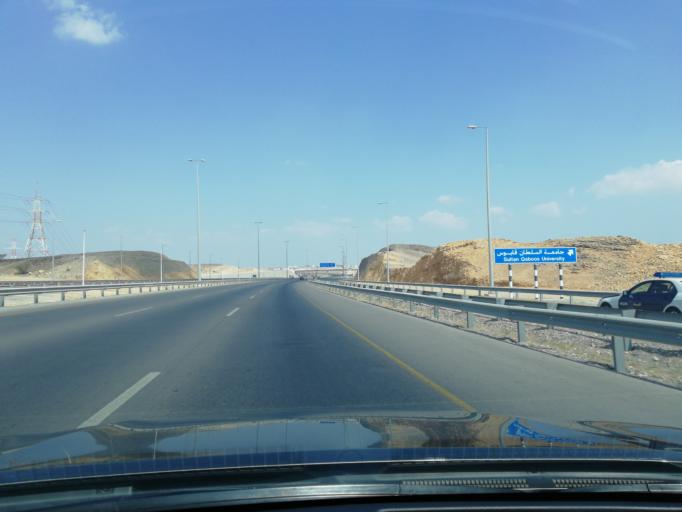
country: OM
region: Muhafazat Masqat
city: As Sib al Jadidah
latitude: 23.5752
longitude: 58.1450
